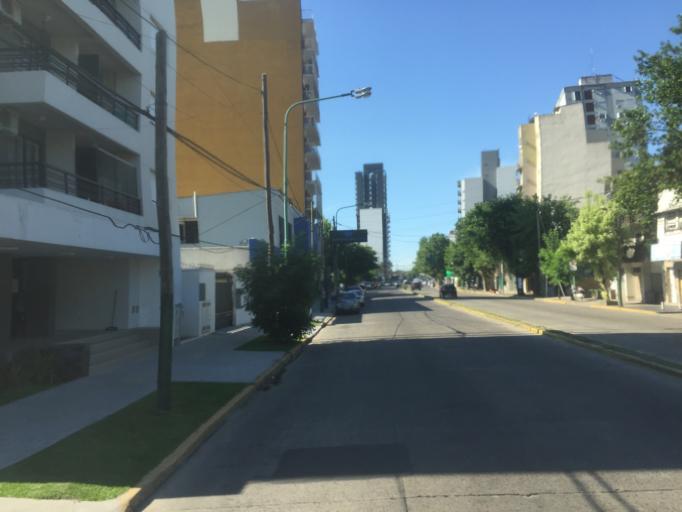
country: AR
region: Buenos Aires
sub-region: Partido de Lomas de Zamora
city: Lomas de Zamora
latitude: -34.7659
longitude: -58.3966
